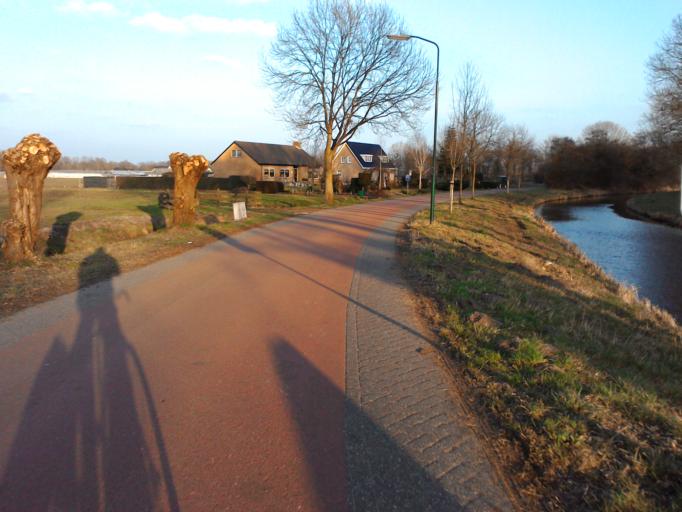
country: NL
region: Utrecht
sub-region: Stichtse Vecht
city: Maarssen
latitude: 52.1369
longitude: 5.0604
